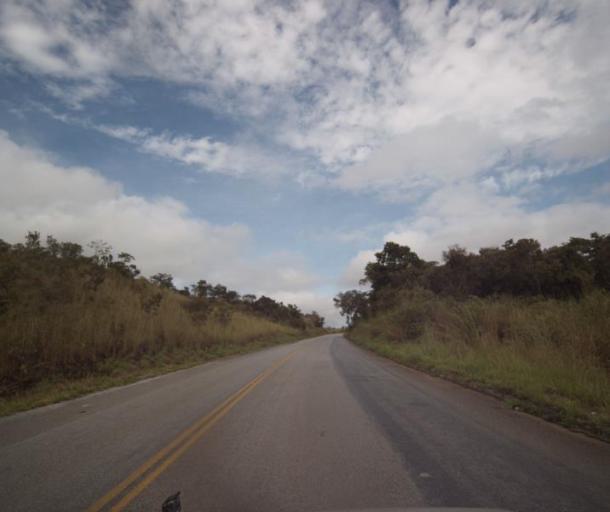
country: BR
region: Goias
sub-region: Pirenopolis
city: Pirenopolis
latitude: -15.7218
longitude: -48.6987
